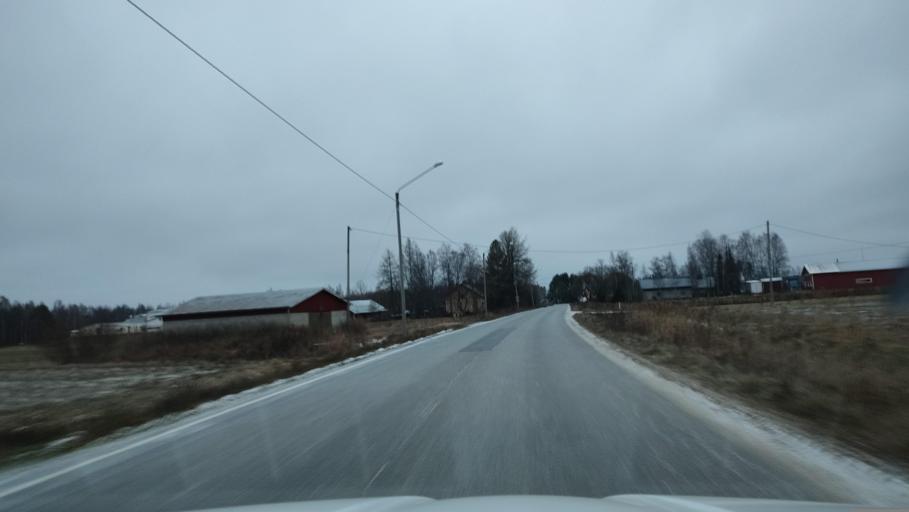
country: FI
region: Southern Ostrobothnia
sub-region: Suupohja
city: Karijoki
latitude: 62.2525
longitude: 21.6753
